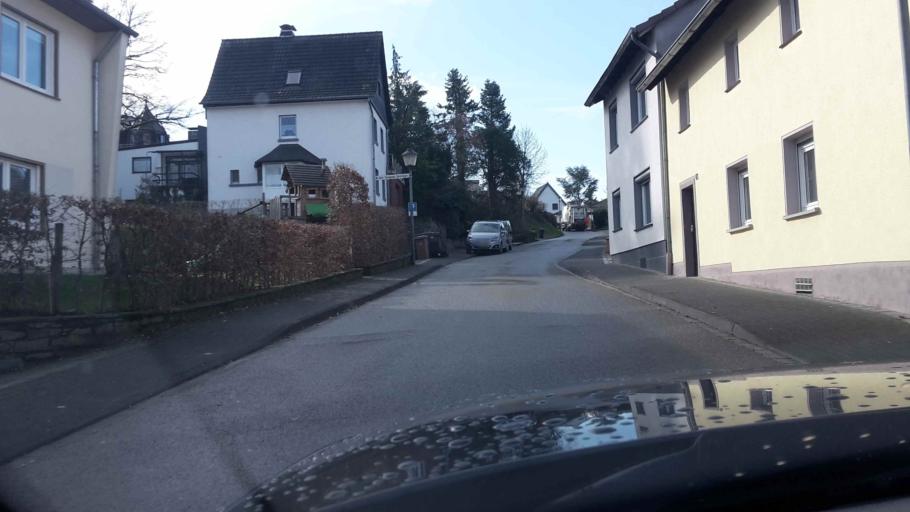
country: DE
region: North Rhine-Westphalia
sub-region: Regierungsbezirk Koln
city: Hennef
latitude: 50.7704
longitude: 7.2689
